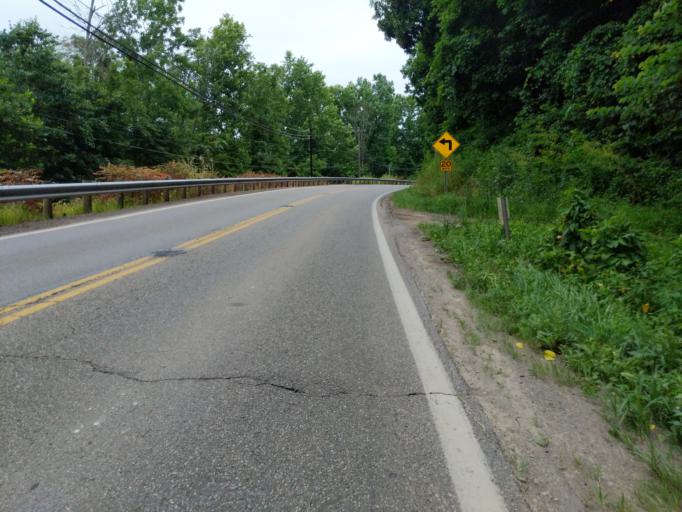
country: US
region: Ohio
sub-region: Athens County
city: Chauncey
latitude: 39.3921
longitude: -82.1414
